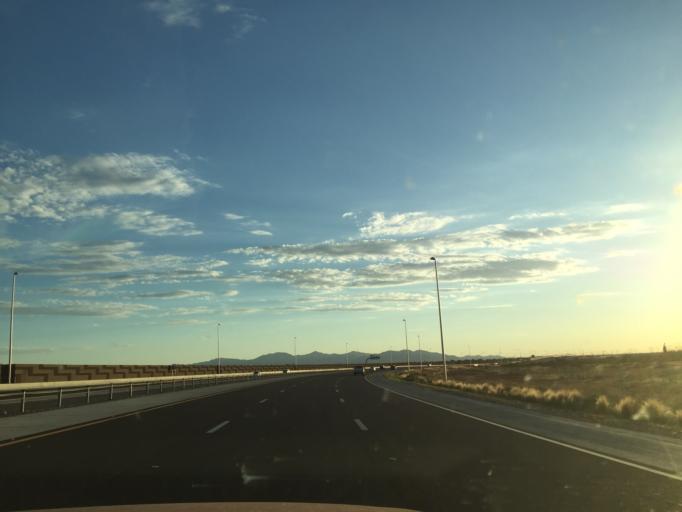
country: US
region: Arizona
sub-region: Maricopa County
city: Sun City West
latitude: 33.7000
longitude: -112.3193
